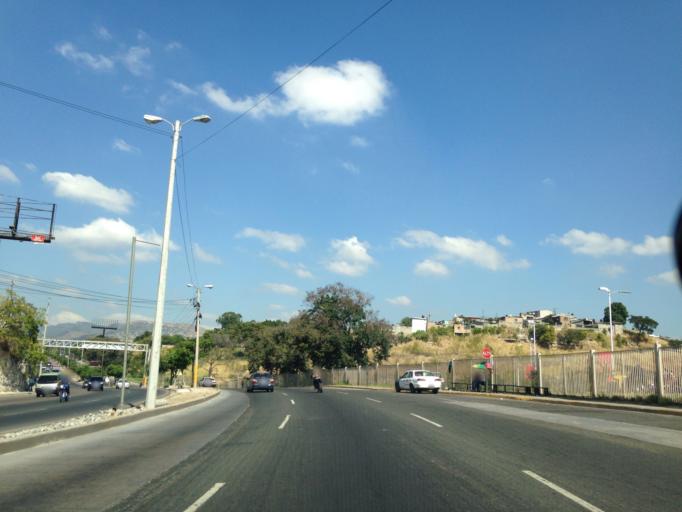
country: HN
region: Francisco Morazan
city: Tegucigalpa
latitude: 14.0747
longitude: -87.2135
